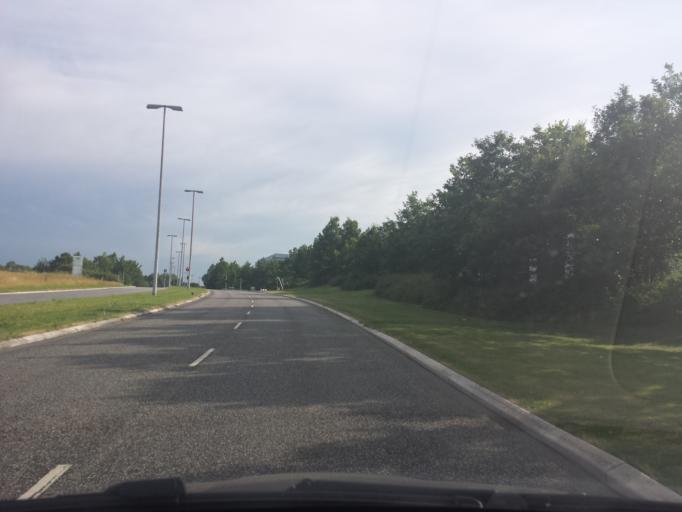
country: DK
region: Capital Region
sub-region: Ballerup Kommune
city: Ballerup
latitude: 55.7403
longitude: 12.3916
